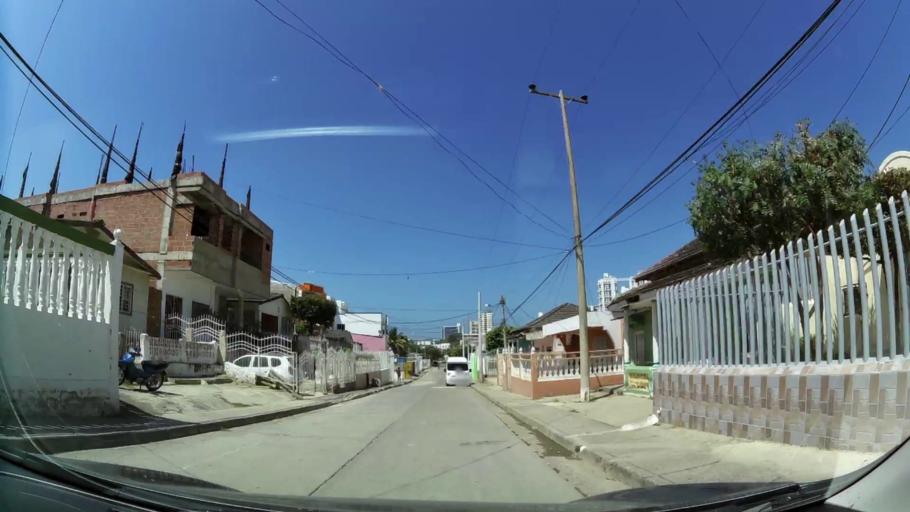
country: CO
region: Bolivar
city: Cartagena
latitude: 10.4292
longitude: -75.5321
